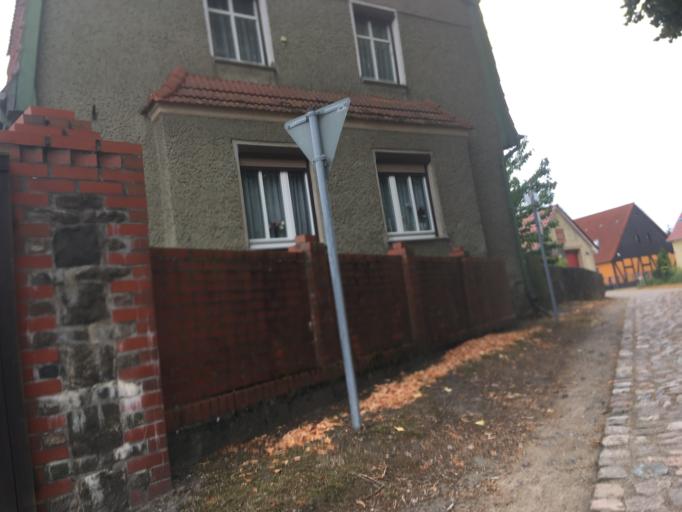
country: DE
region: Brandenburg
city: Chorin
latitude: 52.9323
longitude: 13.8589
